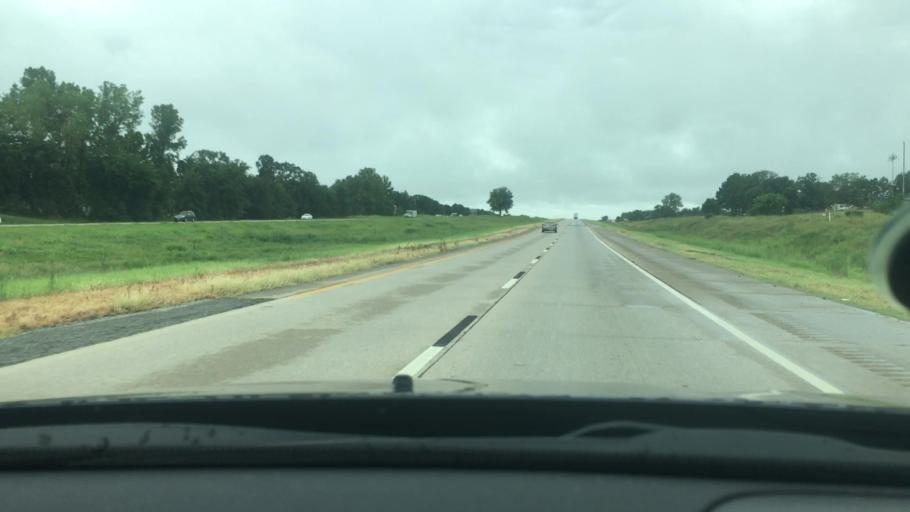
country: US
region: Oklahoma
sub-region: Atoka County
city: Atoka
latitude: 34.2106
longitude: -96.2338
